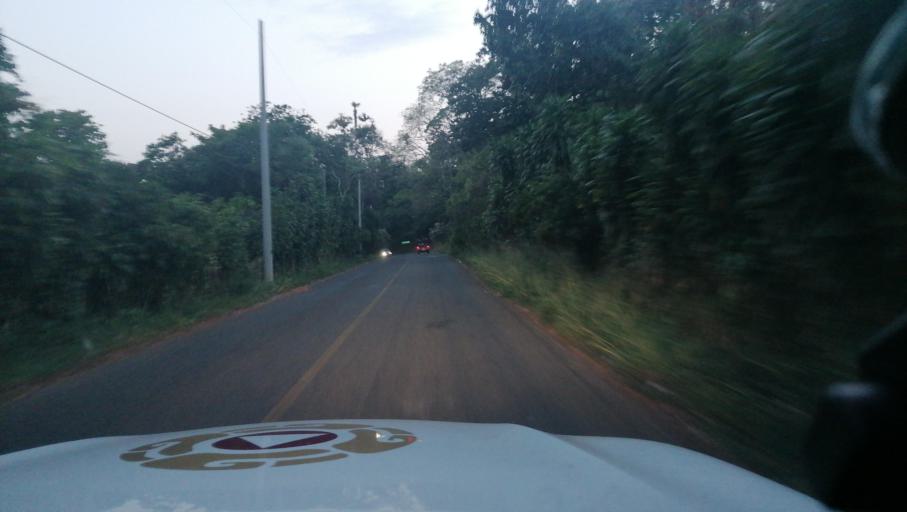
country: MX
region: Chiapas
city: Veinte de Noviembre
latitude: 15.0092
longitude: -92.2465
